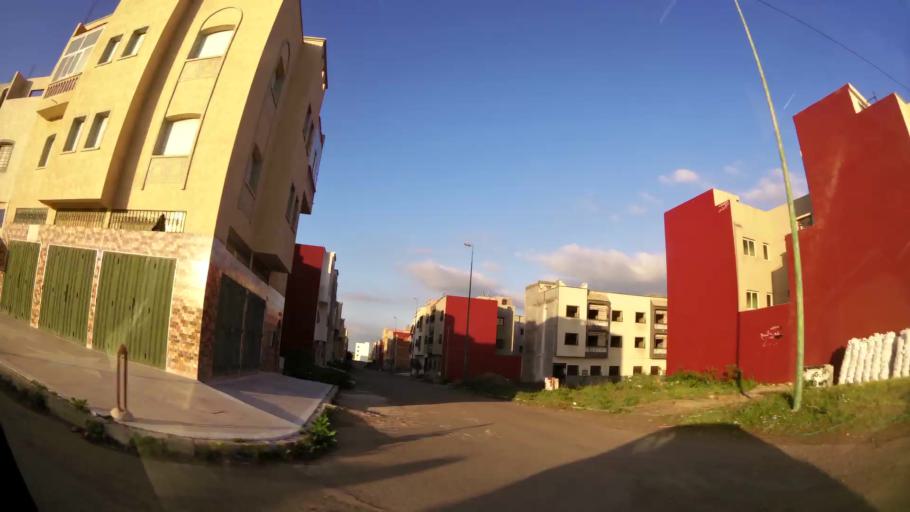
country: MA
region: Chaouia-Ouardigha
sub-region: Settat Province
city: Settat
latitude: 32.9849
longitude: -7.5993
